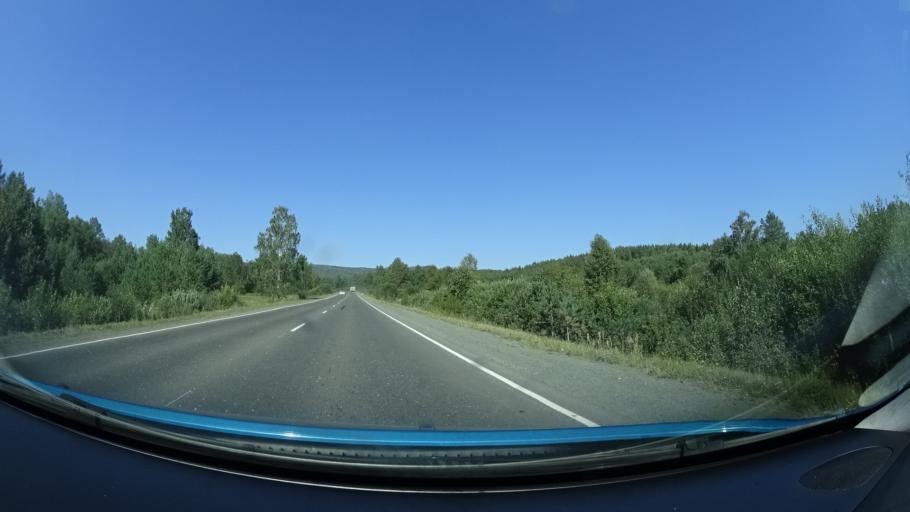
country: RU
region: Bashkortostan
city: Abzakovo
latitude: 53.8585
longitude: 58.5612
